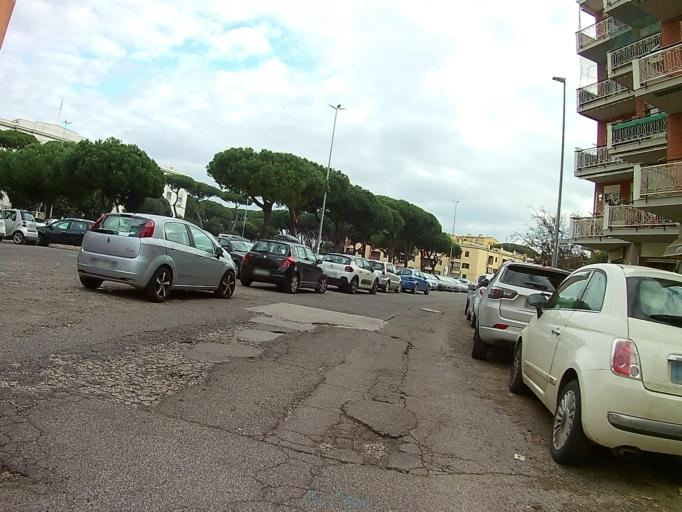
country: IT
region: Latium
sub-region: Citta metropolitana di Roma Capitale
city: Lido di Ostia
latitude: 41.7306
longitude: 12.2932
